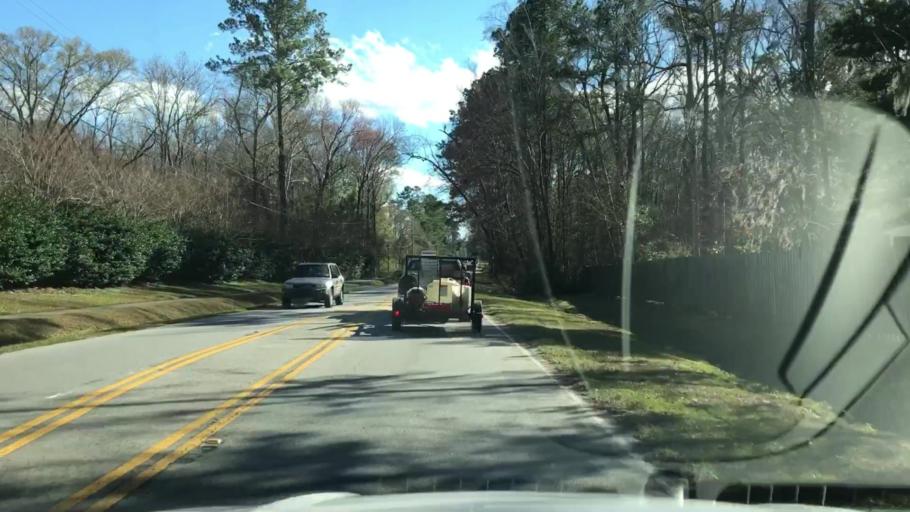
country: US
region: South Carolina
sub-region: Dorchester County
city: Summerville
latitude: 33.0291
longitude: -80.2445
